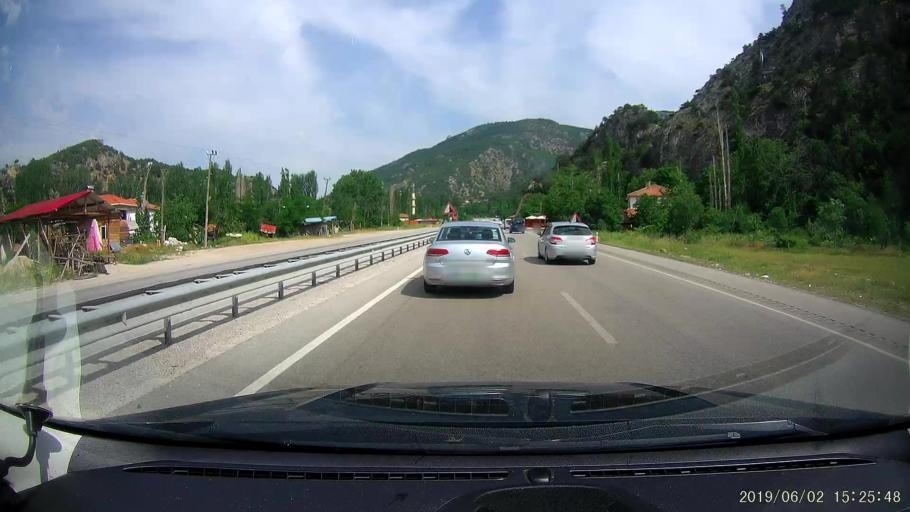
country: TR
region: Amasya
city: Saraycik
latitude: 40.9906
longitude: 35.0267
